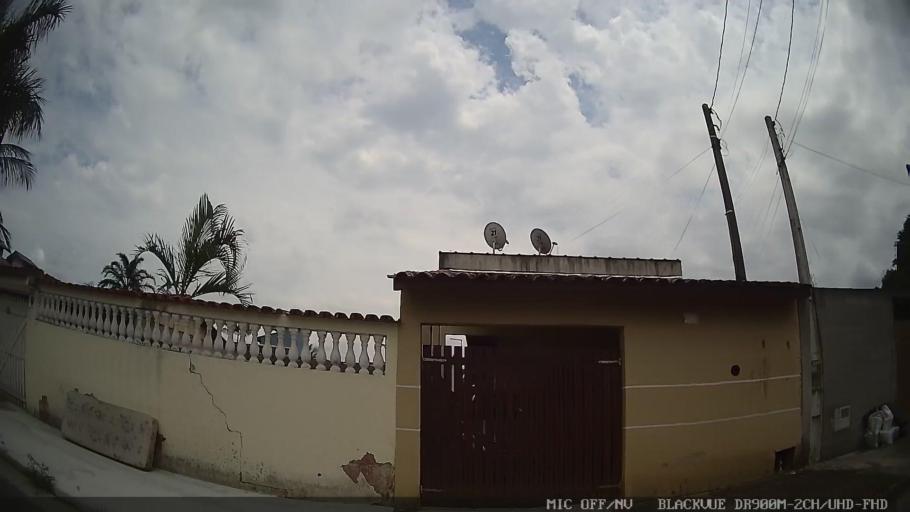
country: BR
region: Sao Paulo
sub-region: Caraguatatuba
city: Caraguatatuba
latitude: -23.6728
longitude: -45.4448
